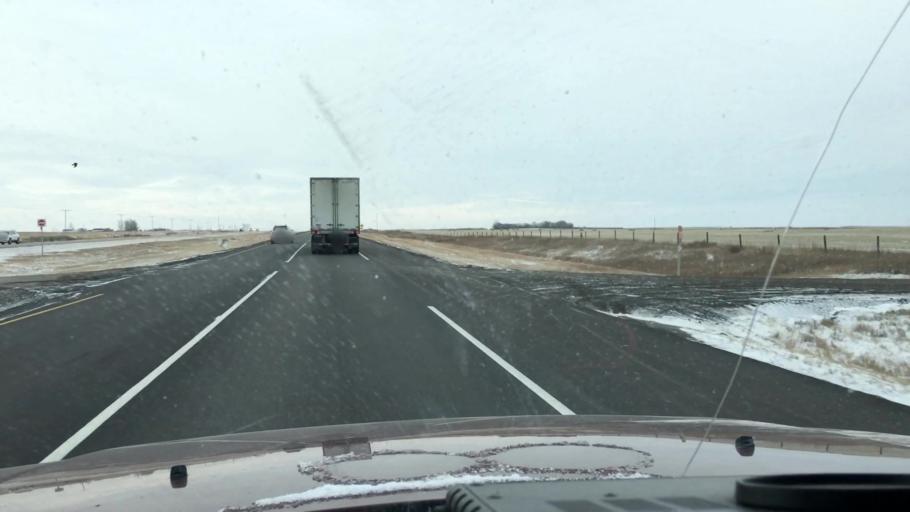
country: CA
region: Saskatchewan
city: Saskatoon
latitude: 51.7946
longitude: -106.4861
